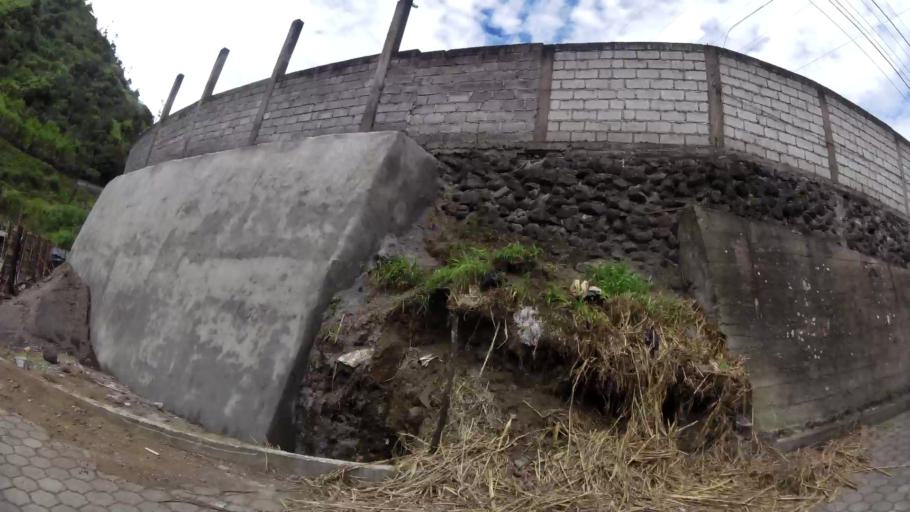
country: EC
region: Tungurahua
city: Banos
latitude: -1.3979
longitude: -78.3954
